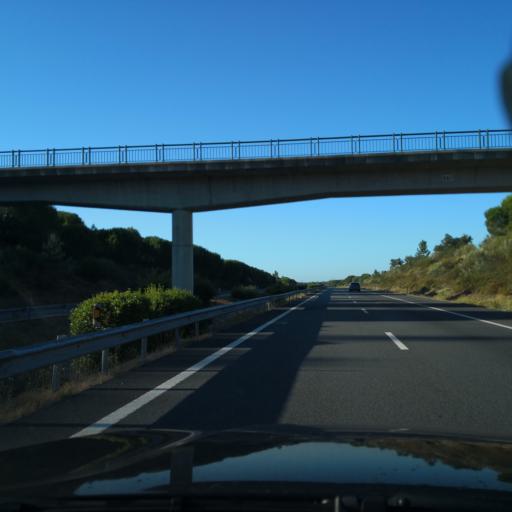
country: PT
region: Evora
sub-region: Vendas Novas
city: Vendas Novas
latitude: 38.5622
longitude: -8.6180
